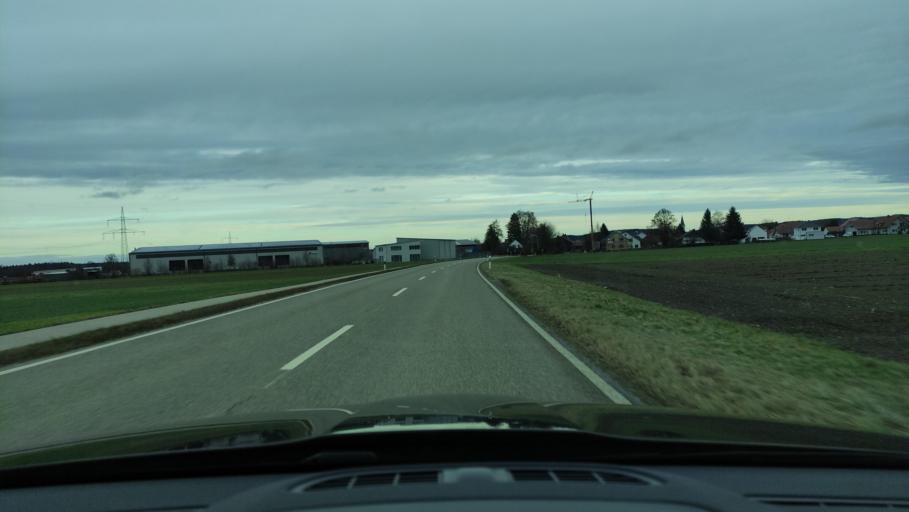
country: DE
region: Bavaria
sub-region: Swabia
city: Breitenthal
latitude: 48.2368
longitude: 10.2862
